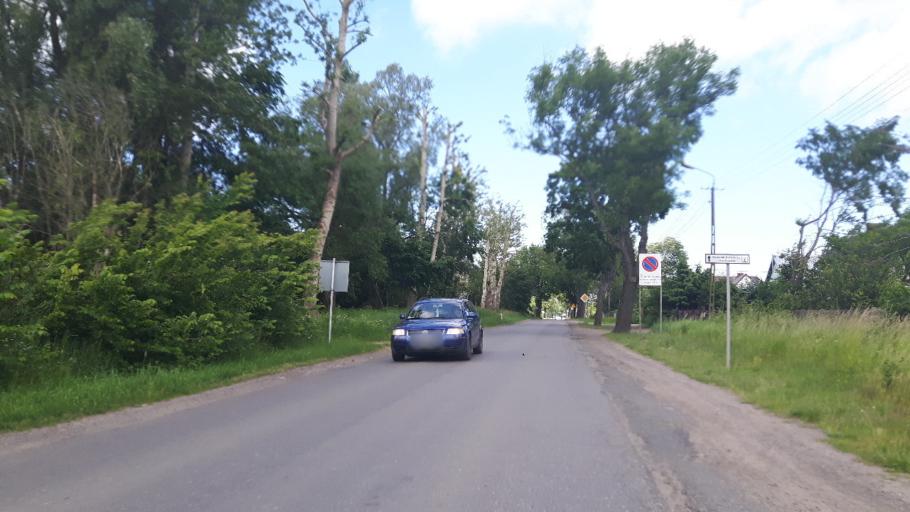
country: PL
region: Pomeranian Voivodeship
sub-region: Powiat slupski
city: Ustka
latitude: 54.5673
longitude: 16.8495
